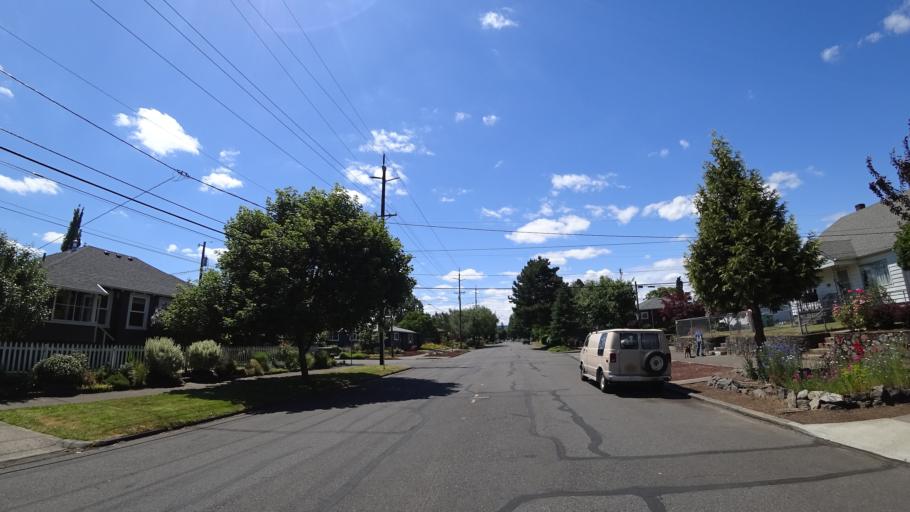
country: US
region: Oregon
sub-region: Multnomah County
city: Portland
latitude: 45.5663
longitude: -122.6860
